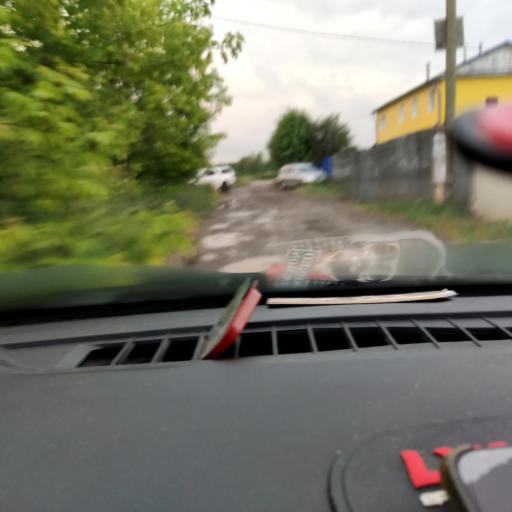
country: RU
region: Perm
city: Froly
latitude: 57.9072
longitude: 56.2692
